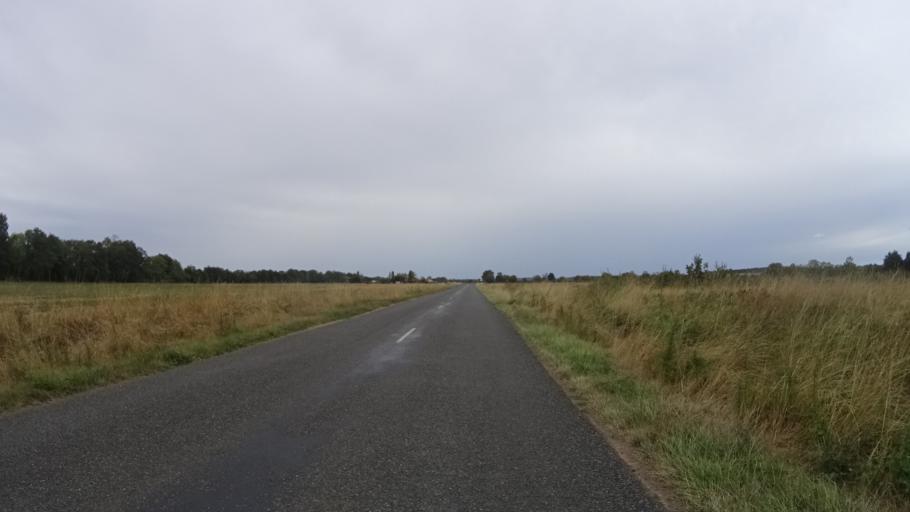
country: FR
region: Bourgogne
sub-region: Departement de la Nievre
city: Decize
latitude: 46.7832
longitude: 3.5337
